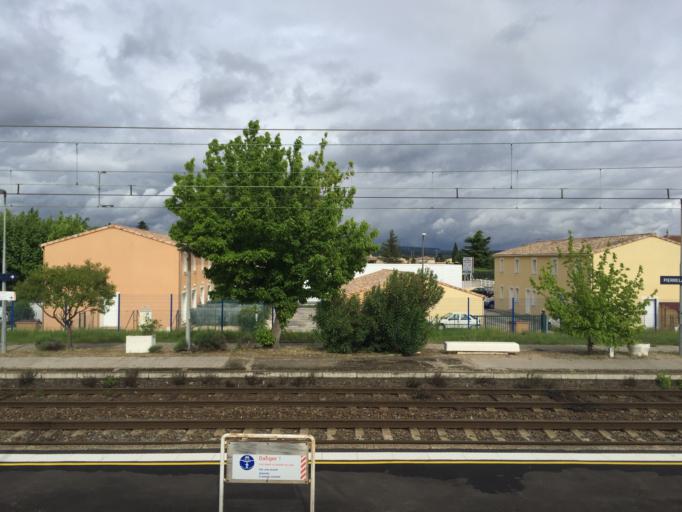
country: FR
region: Rhone-Alpes
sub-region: Departement de la Drome
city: Pierrelatte
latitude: 44.3743
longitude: 4.7037
